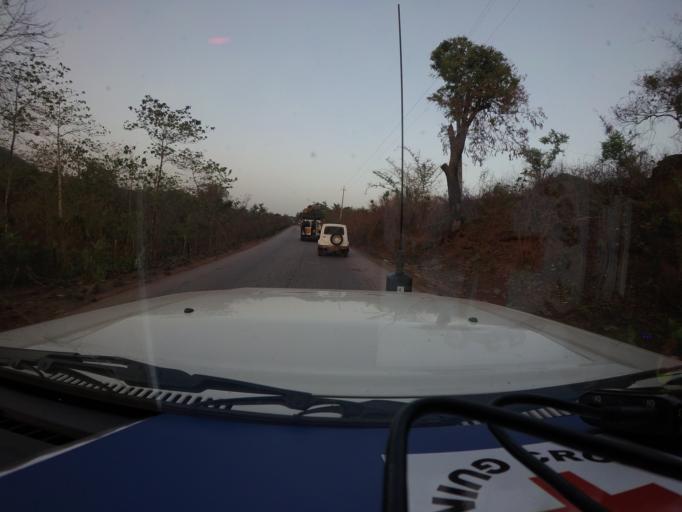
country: GN
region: Kindia
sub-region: Kindia
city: Kindia
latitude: 9.8642
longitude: -13.0688
